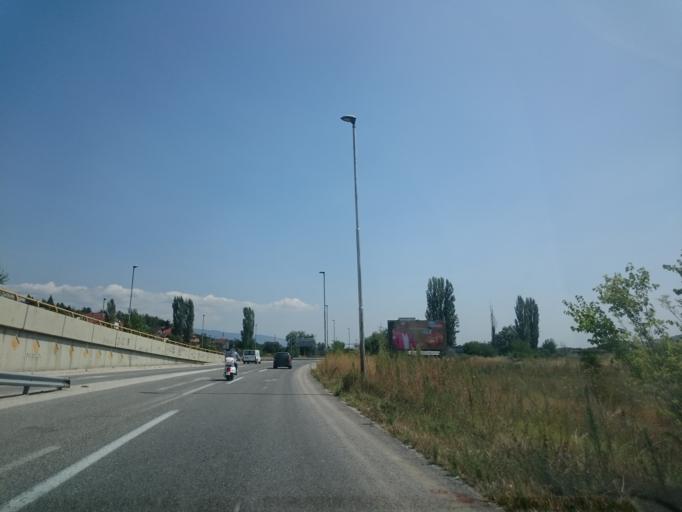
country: MK
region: Saraj
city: Saraj
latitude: 42.0083
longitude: 21.3241
